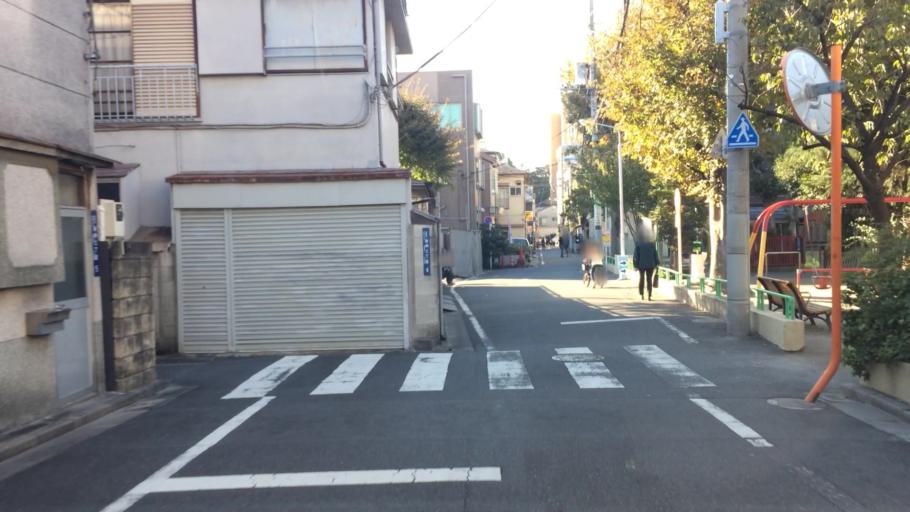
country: JP
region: Tokyo
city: Tokyo
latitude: 35.7255
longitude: 139.7657
